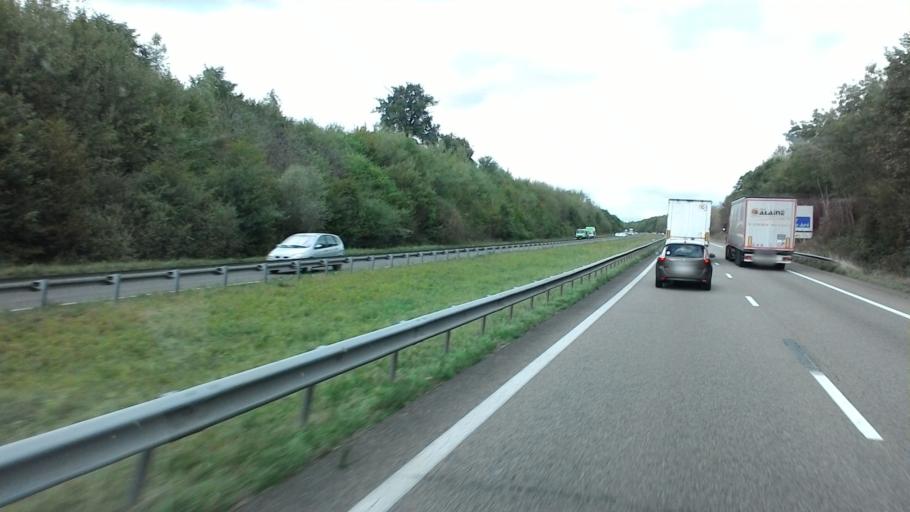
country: FR
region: Lorraine
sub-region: Departement de Meurthe-et-Moselle
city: Pont-a-Mousson
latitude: 48.9042
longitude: 6.1073
